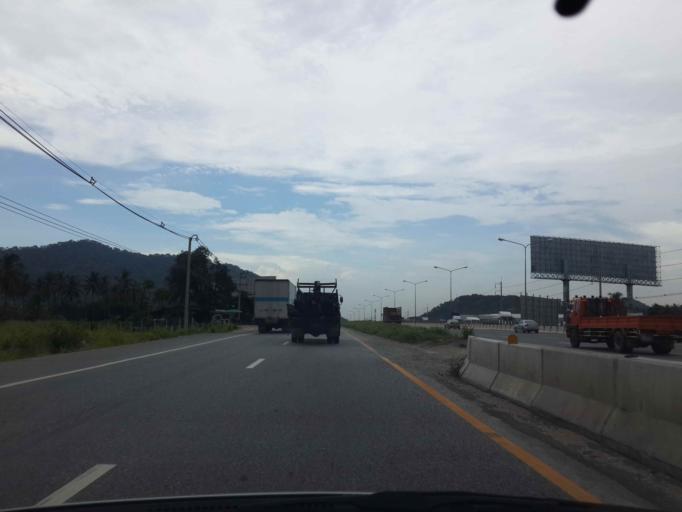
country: TH
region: Chon Buri
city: Si Racha
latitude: 13.2499
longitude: 100.9931
